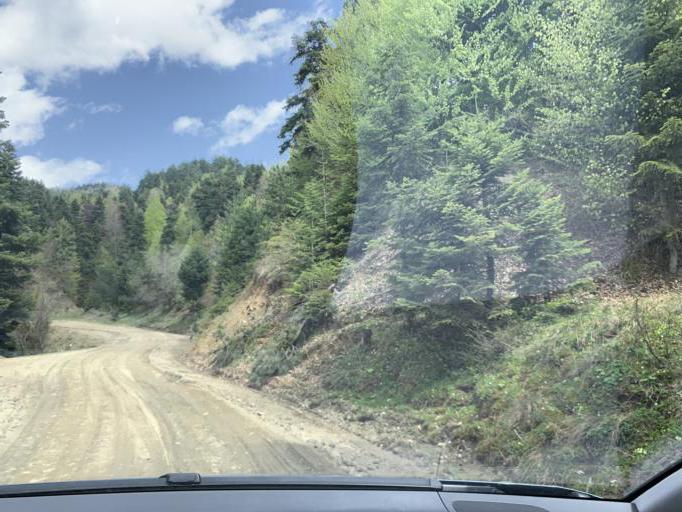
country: TR
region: Bolu
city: Bolu
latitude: 40.8373
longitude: 31.6712
